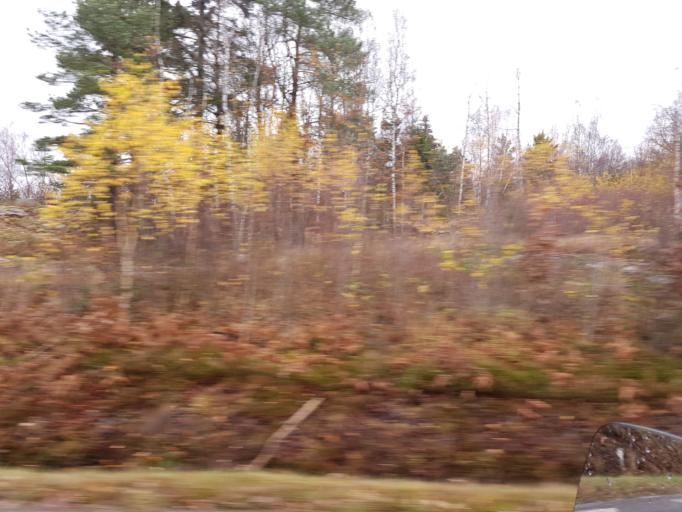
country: SE
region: Vaestra Goetaland
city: Svanesund
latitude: 58.1573
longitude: 11.7843
